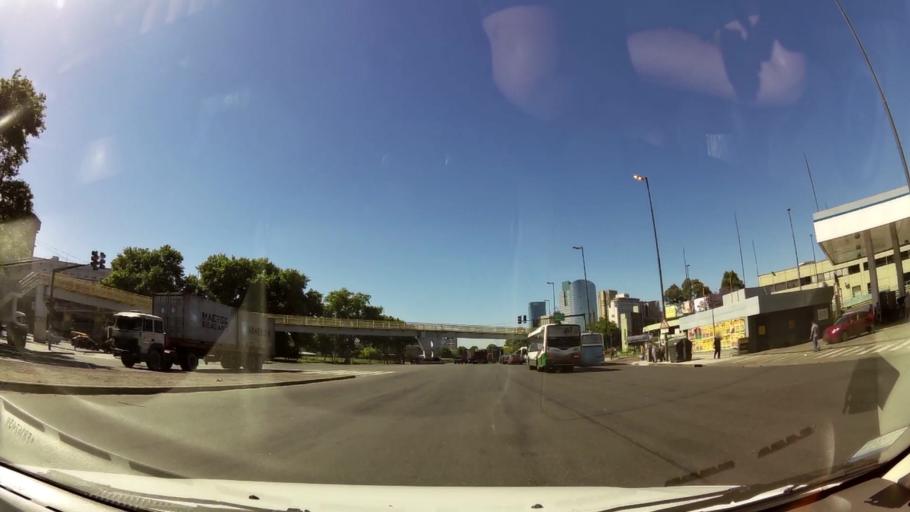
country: AR
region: Buenos Aires F.D.
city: Retiro
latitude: -34.5869
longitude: -58.3721
